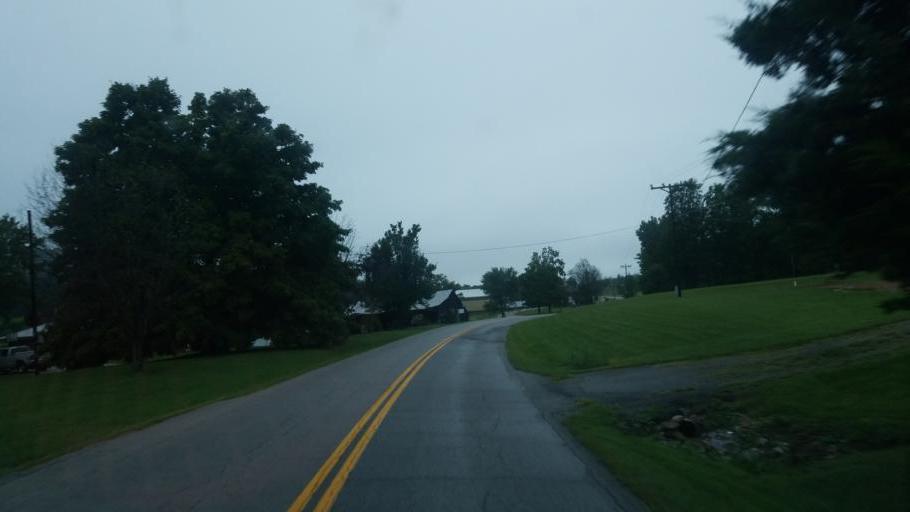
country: US
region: Kentucky
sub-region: Fleming County
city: Flemingsburg
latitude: 38.4049
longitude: -83.6405
